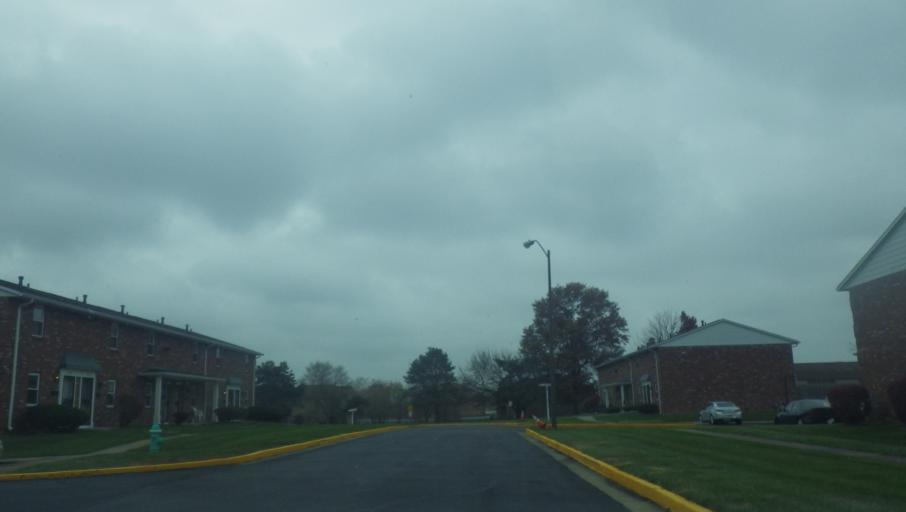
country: US
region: Indiana
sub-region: Marion County
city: Cumberland
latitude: 39.8004
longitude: -85.9930
